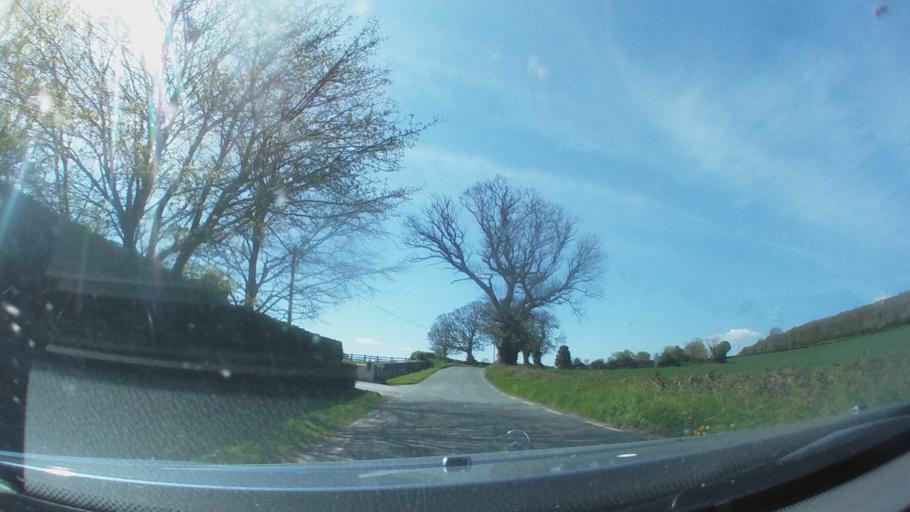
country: IE
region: Leinster
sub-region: Kilkenny
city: Callan
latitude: 52.6102
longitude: -7.3822
